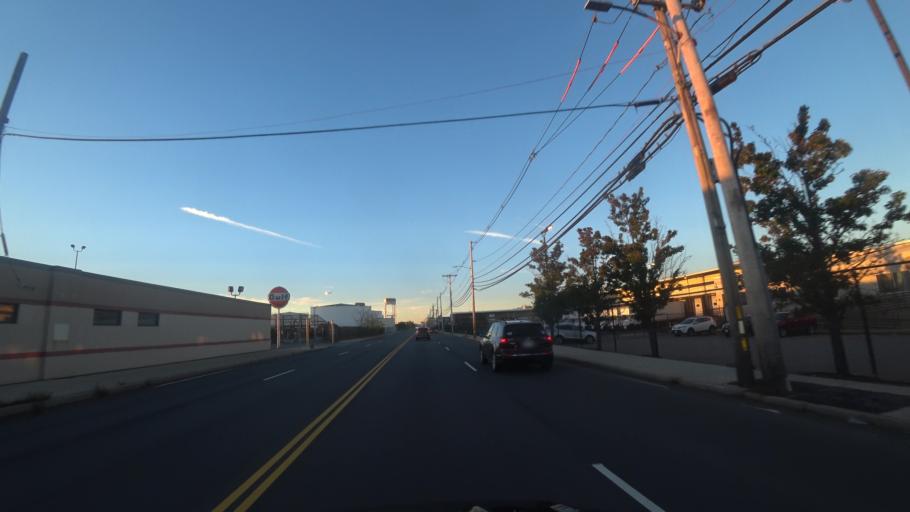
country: US
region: Massachusetts
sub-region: Suffolk County
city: Chelsea
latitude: 42.3953
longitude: -71.0213
